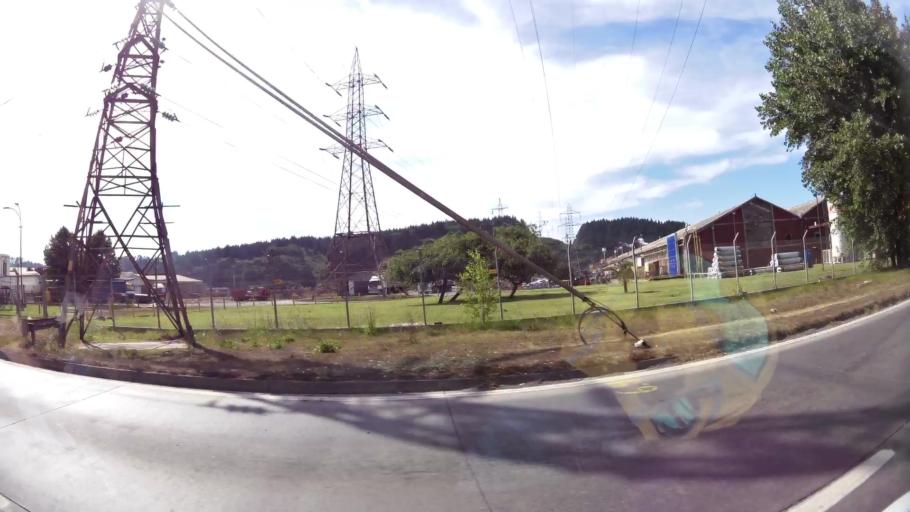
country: CL
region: Biobio
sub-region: Provincia de Concepcion
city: Talcahuano
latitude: -36.7478
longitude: -73.1236
